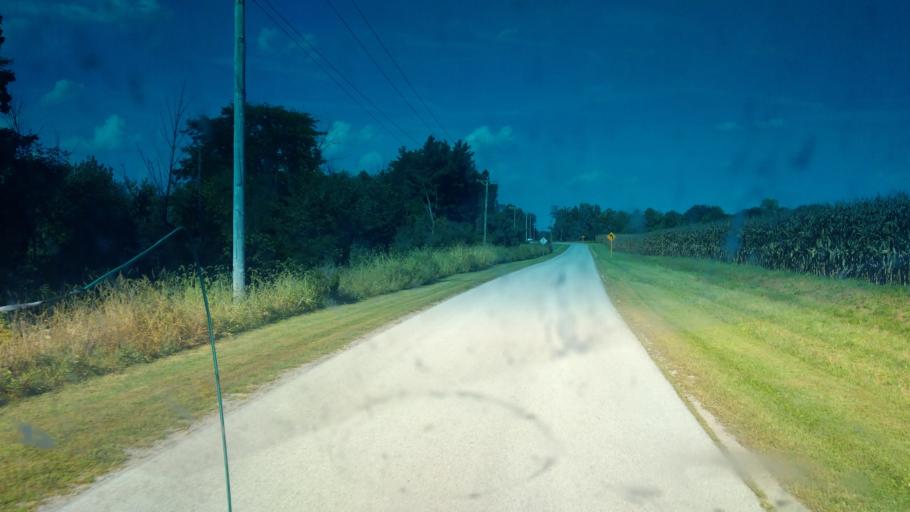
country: US
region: Ohio
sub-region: Hancock County
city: Arlington
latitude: 40.8805
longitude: -83.5705
